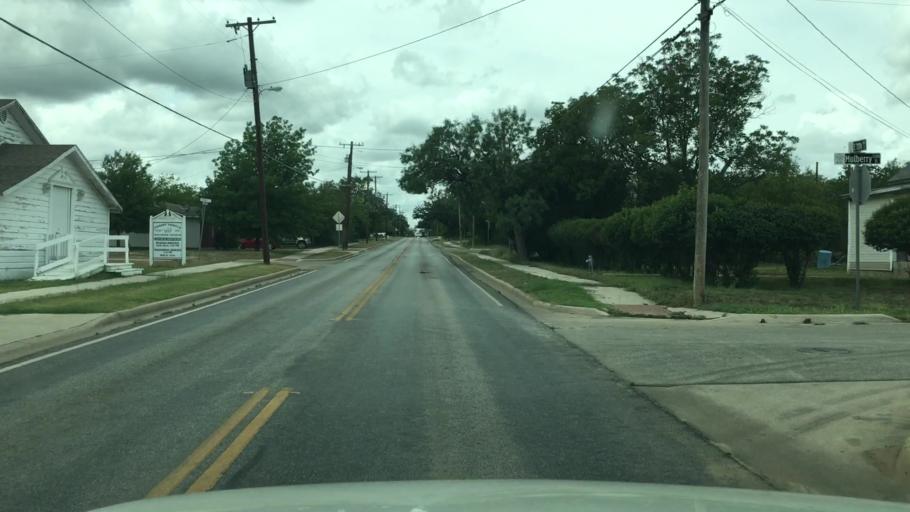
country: US
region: Texas
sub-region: McCulloch County
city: Brady
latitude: 31.1261
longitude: -99.3290
